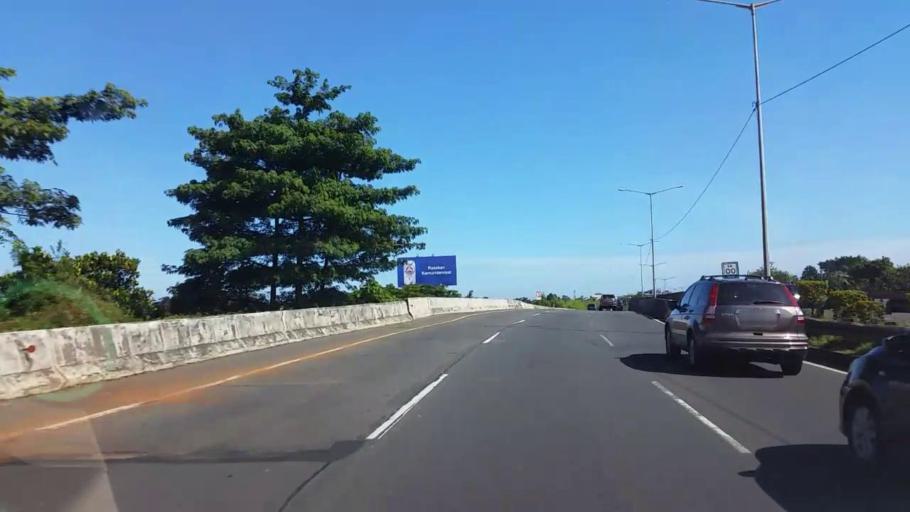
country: ID
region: Banten
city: South Tangerang
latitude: -6.2567
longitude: 106.7606
